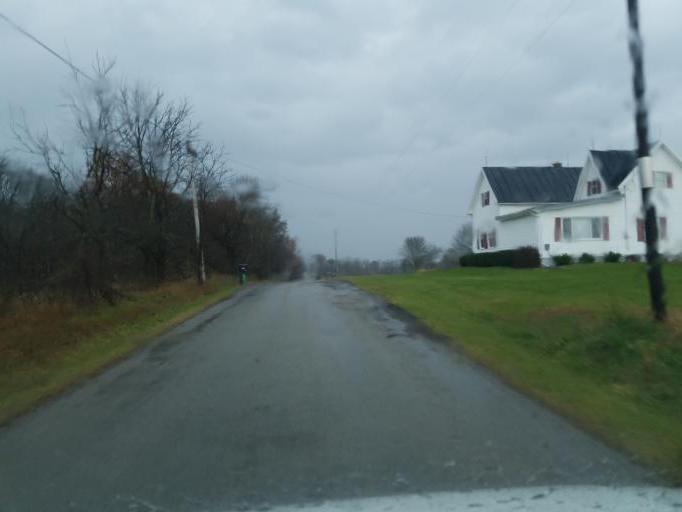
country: US
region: Ohio
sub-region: Morrow County
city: Cardington
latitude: 40.4791
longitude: -82.8793
